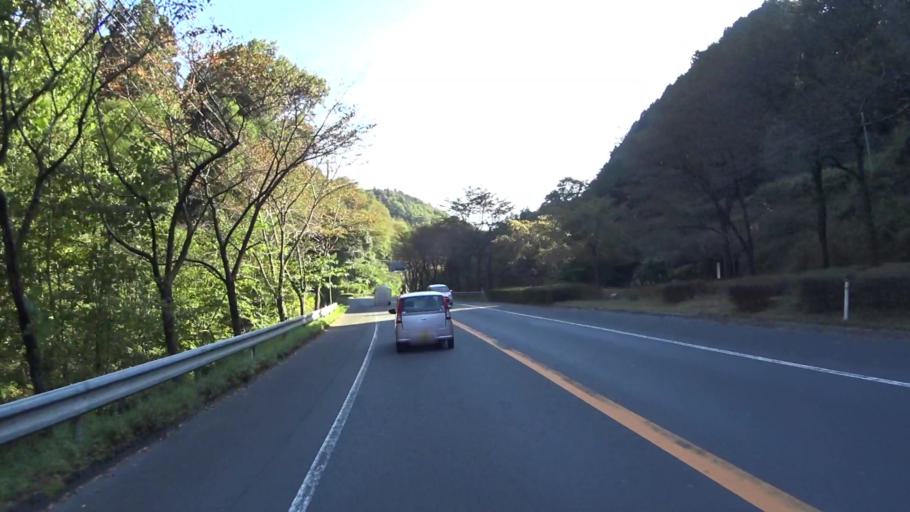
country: JP
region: Kyoto
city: Miyazu
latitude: 35.5465
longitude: 135.1105
